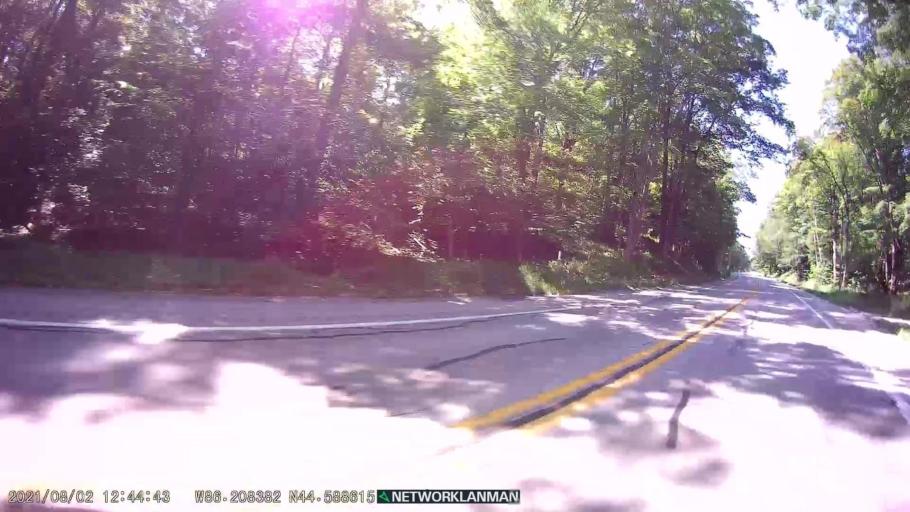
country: US
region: Michigan
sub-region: Benzie County
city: Frankfort
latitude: 44.5888
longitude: -86.2086
